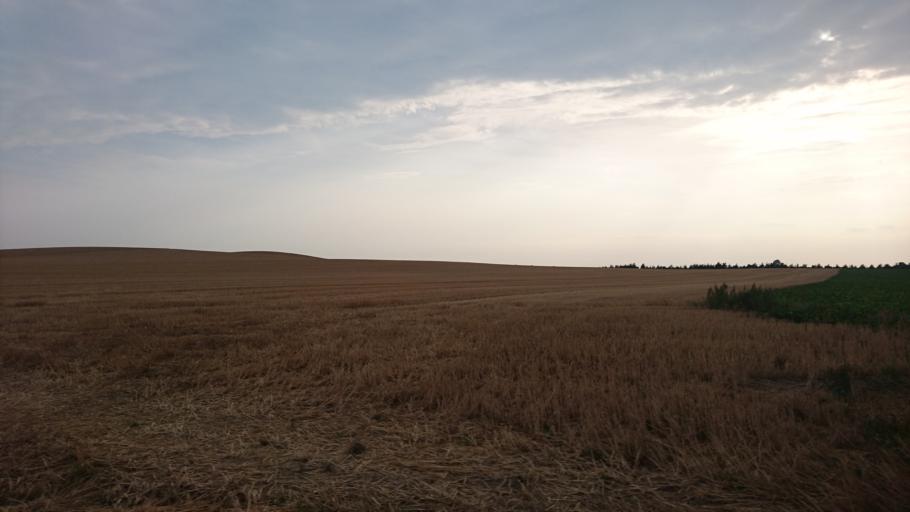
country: DK
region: Zealand
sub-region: Vordingborg Kommune
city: Stege
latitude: 54.9802
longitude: 12.4389
